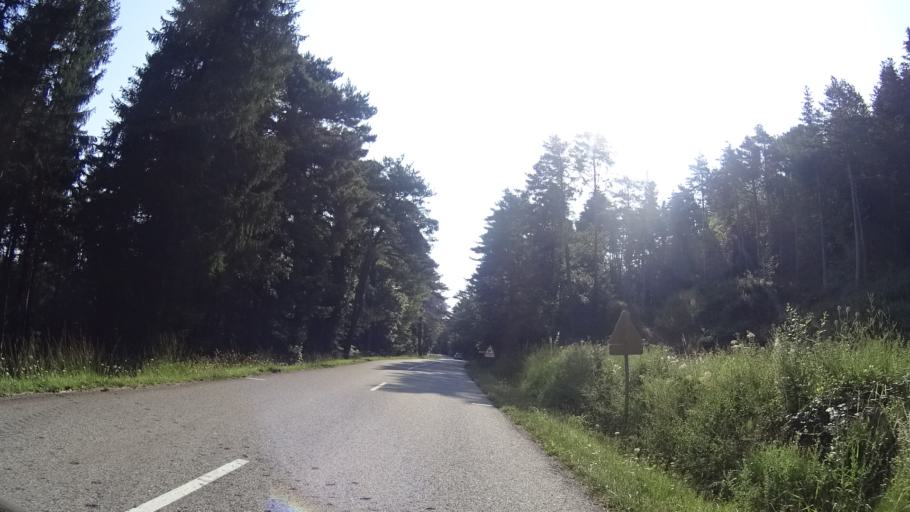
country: FR
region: Midi-Pyrenees
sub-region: Departement de l'Ariege
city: Belesta
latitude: 42.9115
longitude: 1.9894
